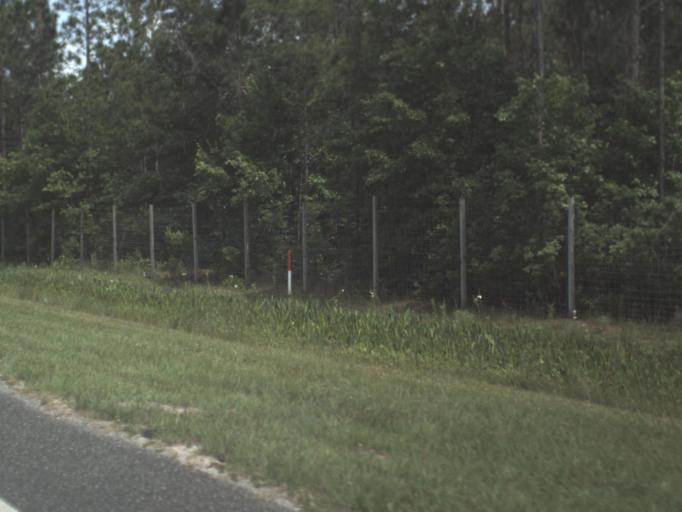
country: US
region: Florida
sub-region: Putnam County
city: Interlachen
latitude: 29.6271
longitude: -81.7798
